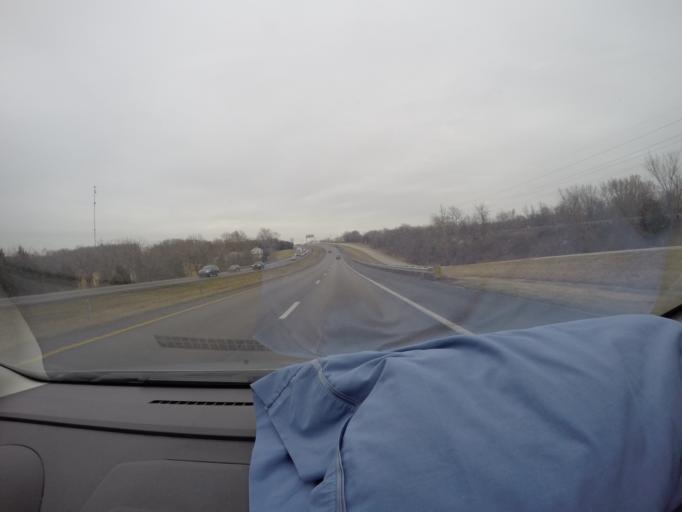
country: US
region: Missouri
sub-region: Warren County
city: Warrenton
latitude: 38.8213
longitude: -91.1893
